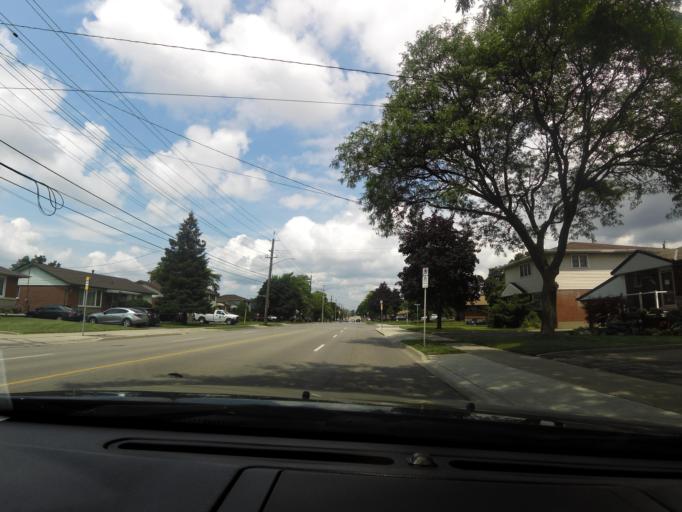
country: CA
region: Ontario
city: Hamilton
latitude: 43.2198
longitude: -79.8319
